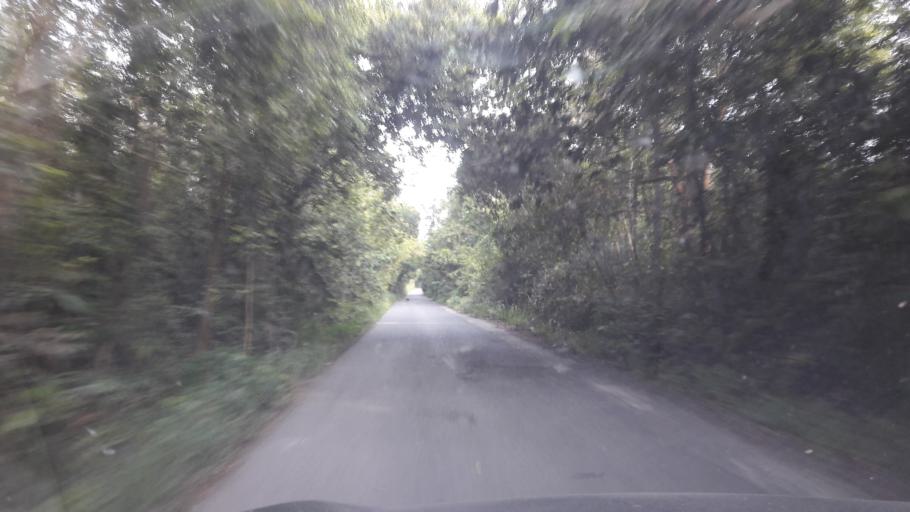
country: ID
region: South Sumatra
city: Gunungmenang
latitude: -3.2756
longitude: 104.0786
